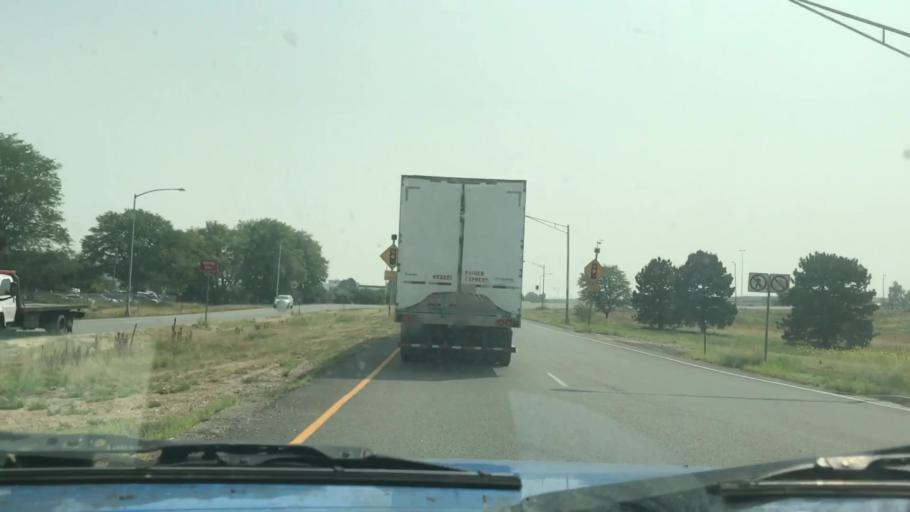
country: US
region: Colorado
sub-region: Adams County
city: Aurora
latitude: 39.7769
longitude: -104.8655
